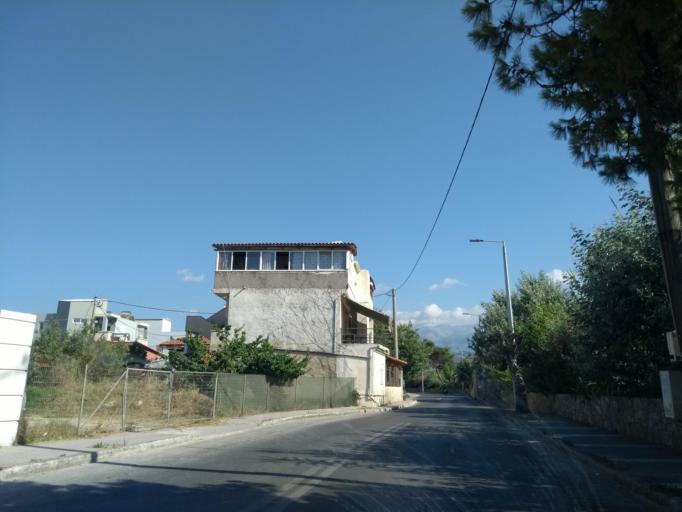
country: GR
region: Crete
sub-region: Nomos Chanias
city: Perivolia
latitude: 35.5101
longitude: 24.0025
